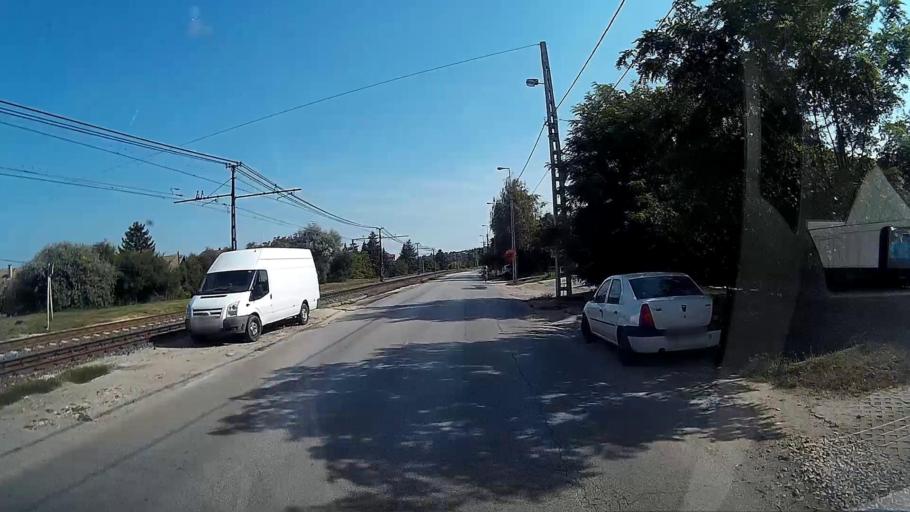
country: HU
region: Pest
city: Budakalasz
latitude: 47.6280
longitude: 19.0435
